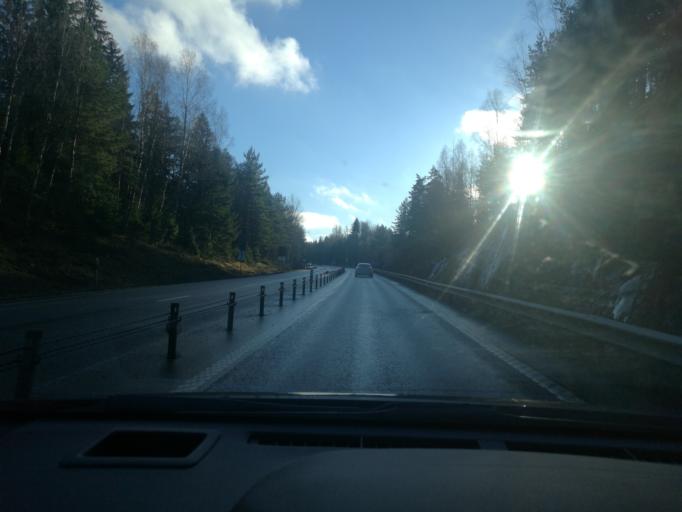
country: SE
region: OEstergoetland
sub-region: Norrkopings Kommun
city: Jursla
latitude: 58.7417
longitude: 16.1728
